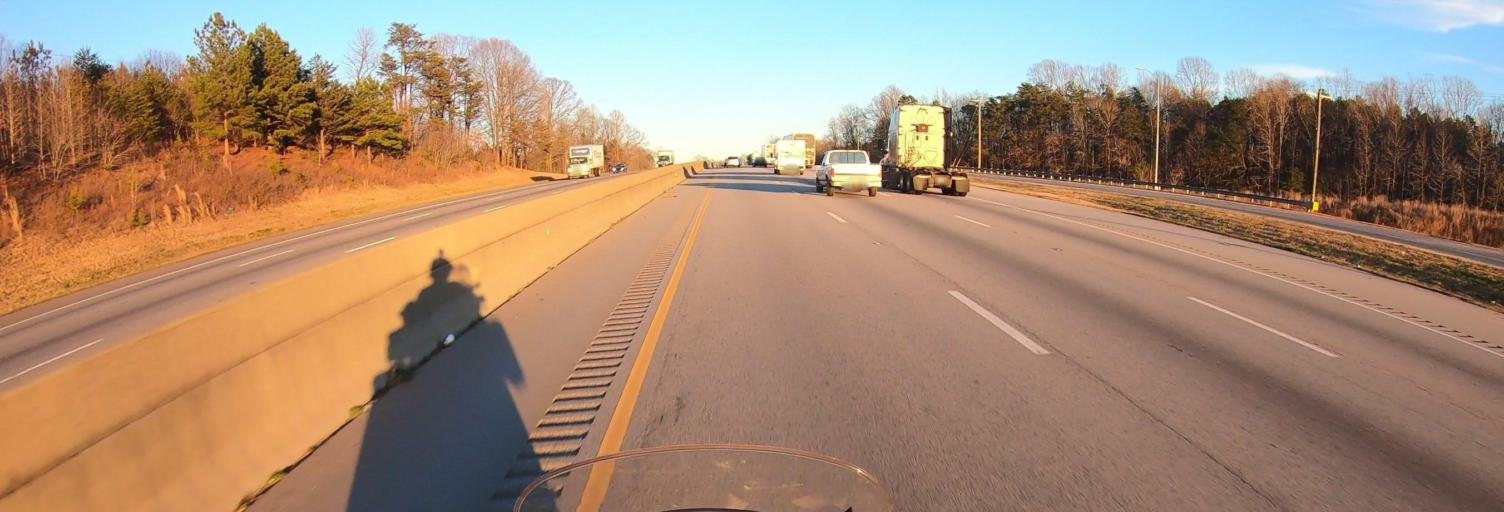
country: US
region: North Carolina
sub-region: Gaston County
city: Bessemer City
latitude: 35.2603
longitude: -81.2748
